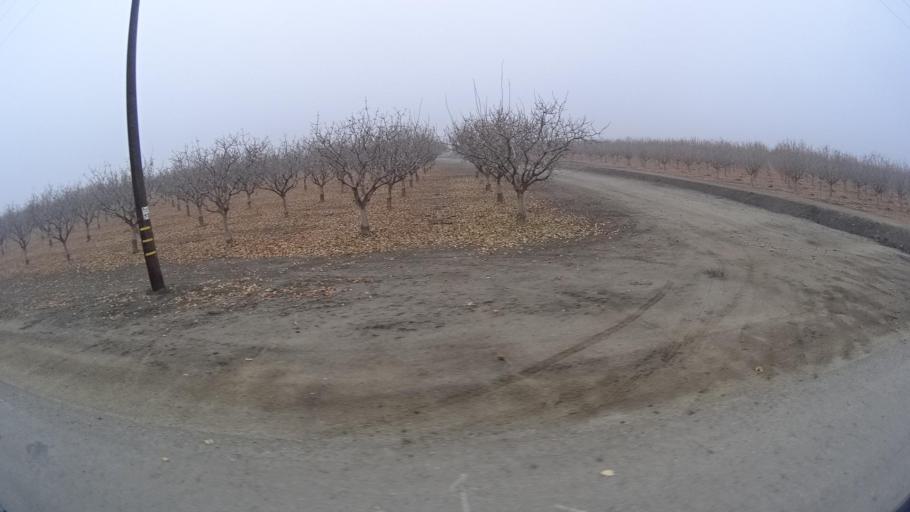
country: US
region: California
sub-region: Kern County
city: Buttonwillow
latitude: 35.4033
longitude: -119.5185
